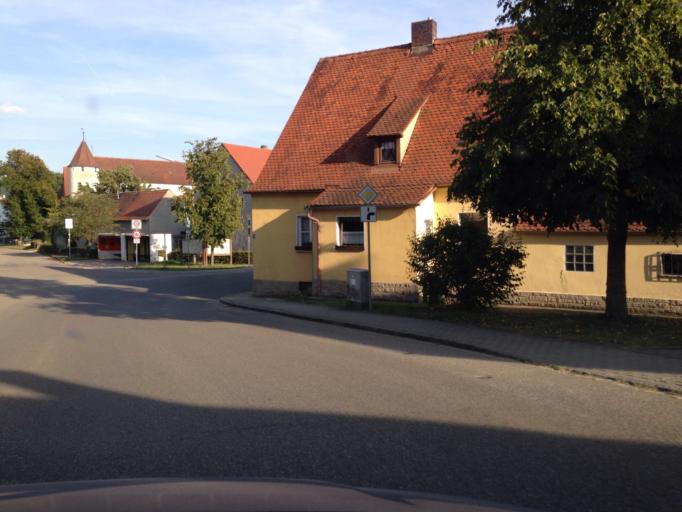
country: DE
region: Bavaria
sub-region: Regierungsbezirk Mittelfranken
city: Thalmassing
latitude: 49.1310
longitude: 11.2116
